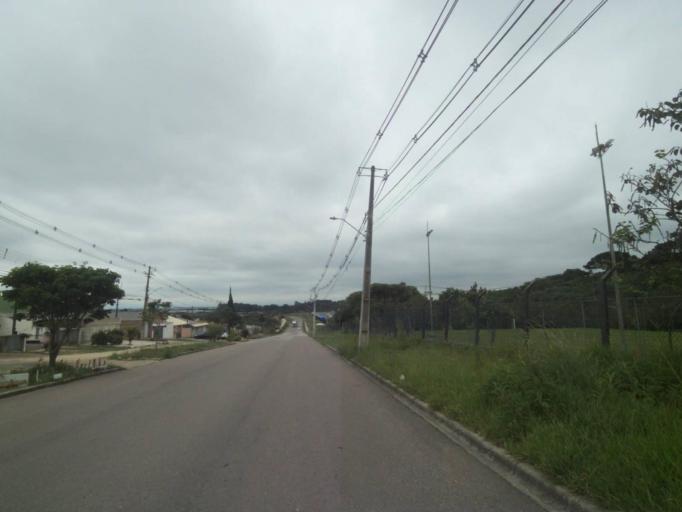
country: BR
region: Parana
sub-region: Araucaria
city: Araucaria
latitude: -25.5589
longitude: -49.3132
